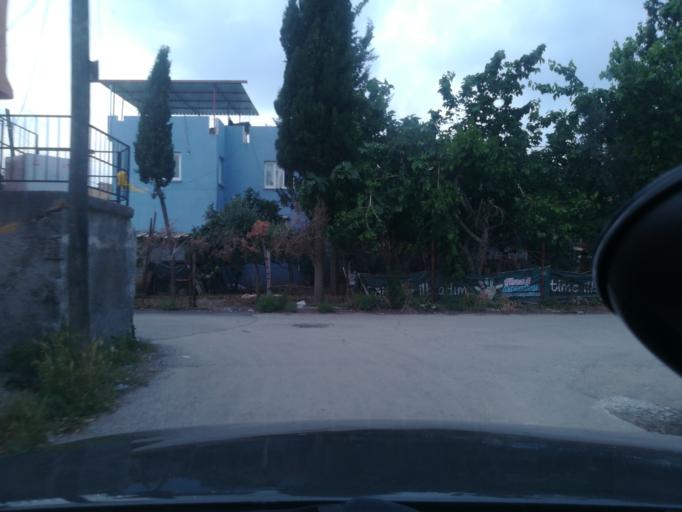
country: TR
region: Adana
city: Seyhan
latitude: 37.0150
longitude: 35.2710
